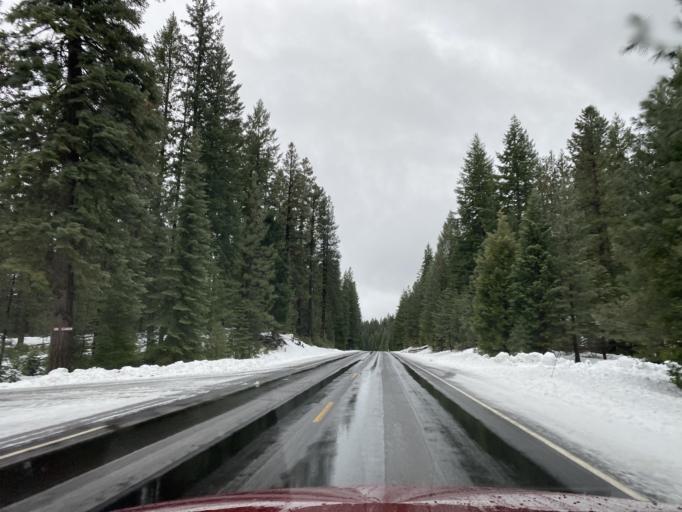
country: US
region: Oregon
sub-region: Klamath County
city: Klamath Falls
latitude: 42.5006
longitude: -122.0836
